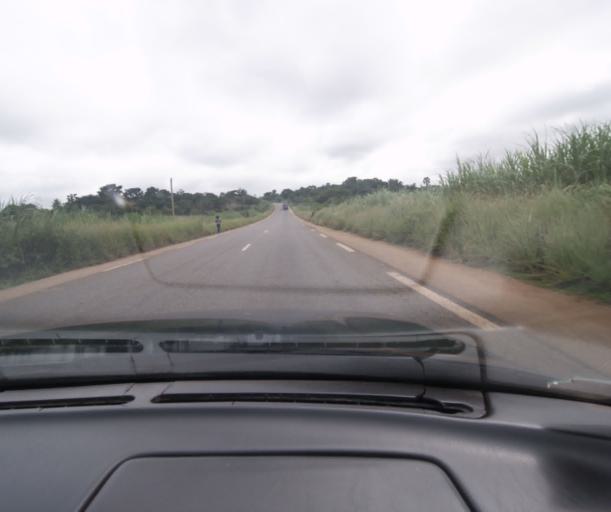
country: CM
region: Centre
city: Ombesa
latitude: 4.5679
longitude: 11.2653
